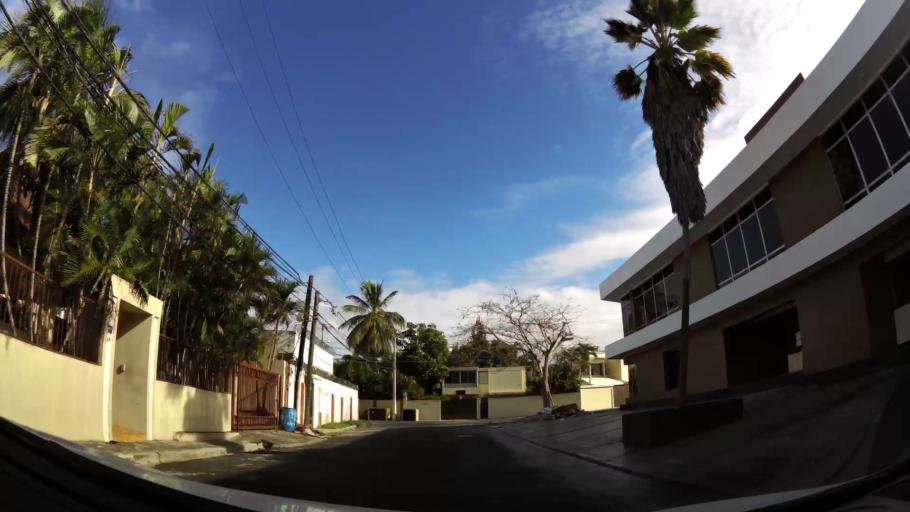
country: DO
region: Nacional
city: La Julia
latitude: 18.4725
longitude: -69.9481
